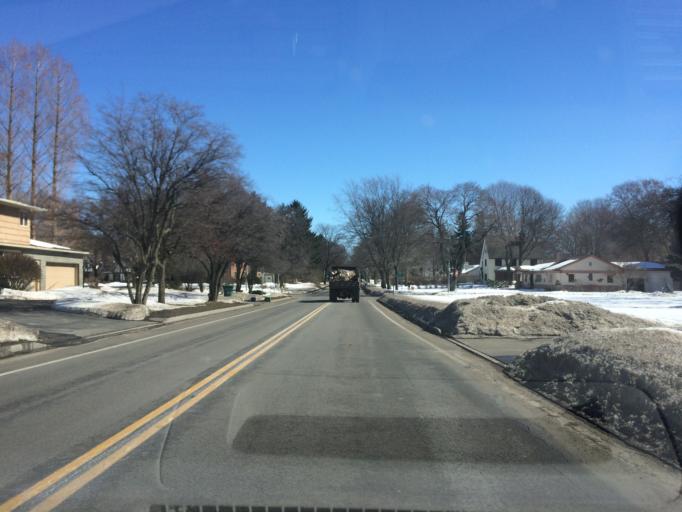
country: US
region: New York
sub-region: Monroe County
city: Brighton
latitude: 43.1372
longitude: -77.5493
